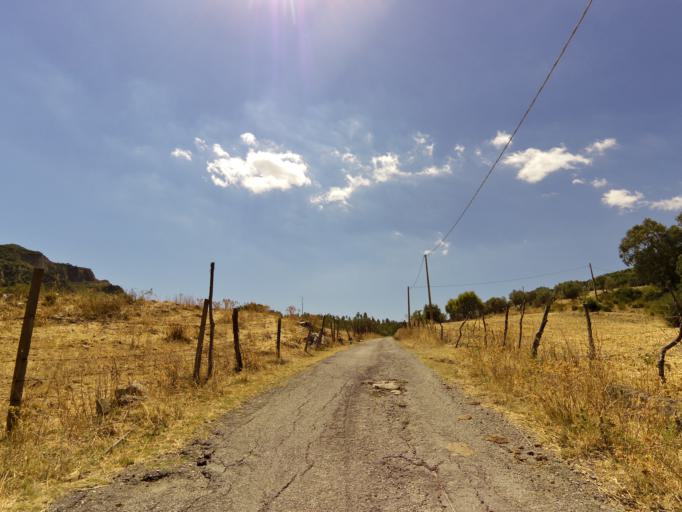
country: IT
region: Calabria
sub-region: Provincia di Reggio Calabria
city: Stilo
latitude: 38.4623
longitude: 16.4672
